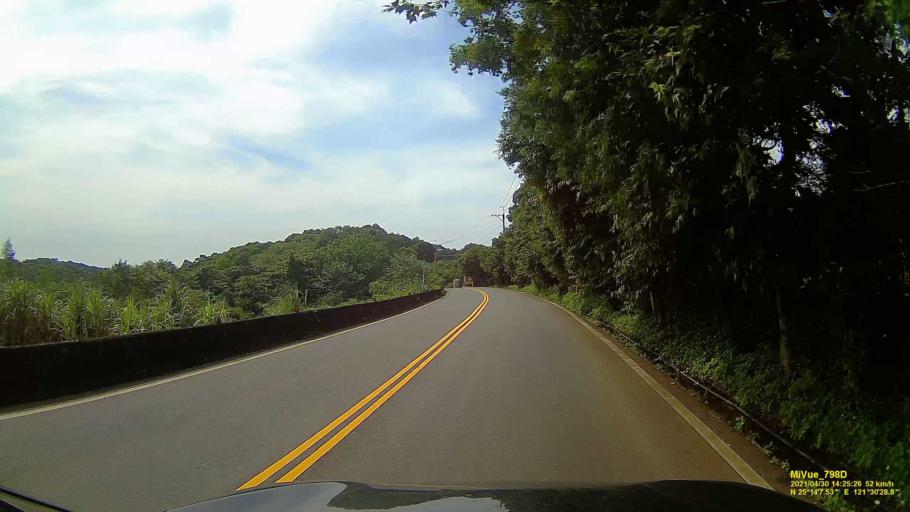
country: TW
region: Taipei
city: Taipei
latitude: 25.2356
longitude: 121.5077
